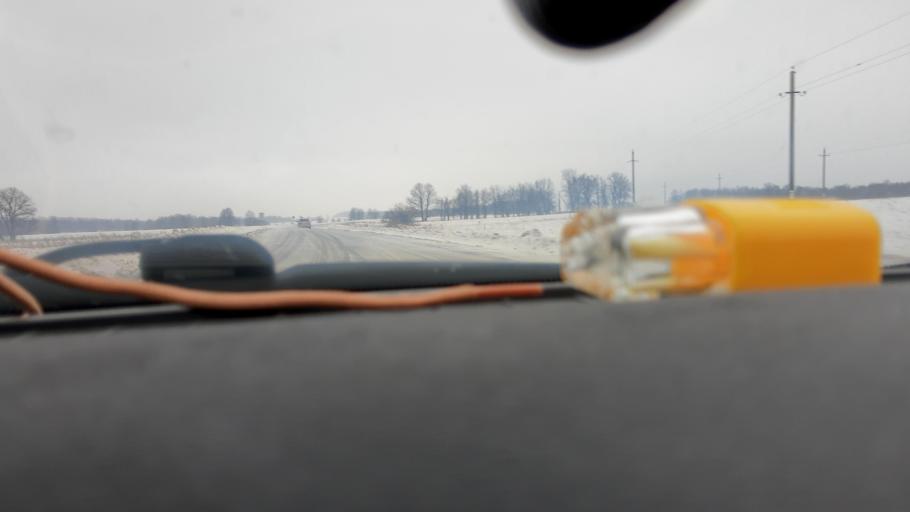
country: RU
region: Bashkortostan
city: Ulukulevo
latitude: 54.5917
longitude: 56.4261
